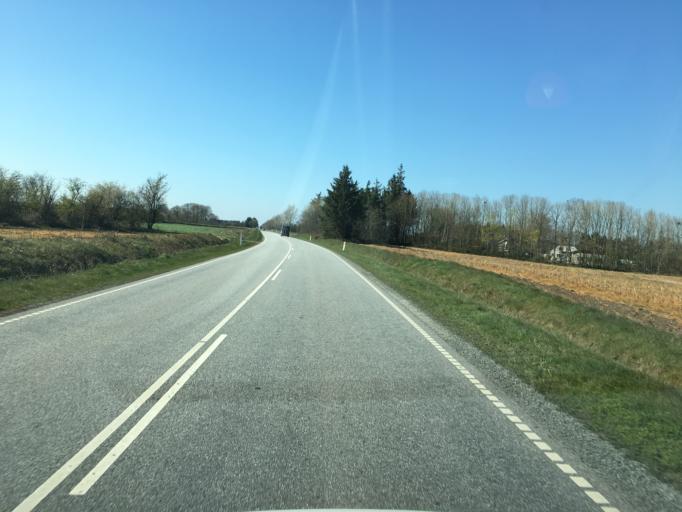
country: DK
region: South Denmark
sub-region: Aabenraa Kommune
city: Krusa
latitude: 54.9420
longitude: 9.3600
